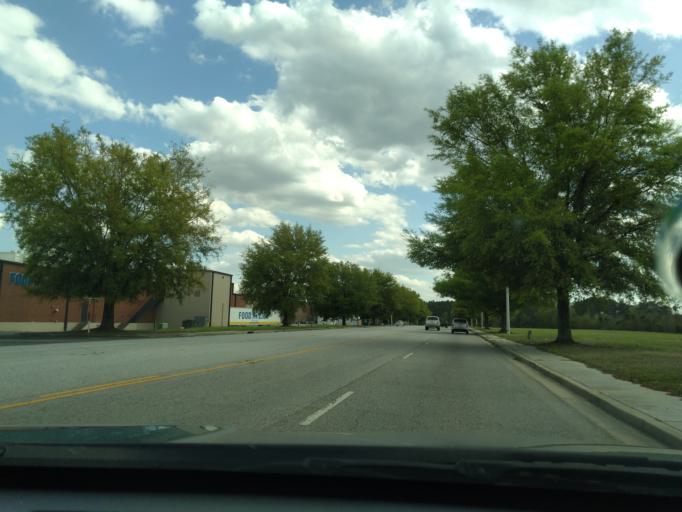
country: US
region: South Carolina
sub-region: Florence County
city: Florence
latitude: 34.1618
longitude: -79.7600
